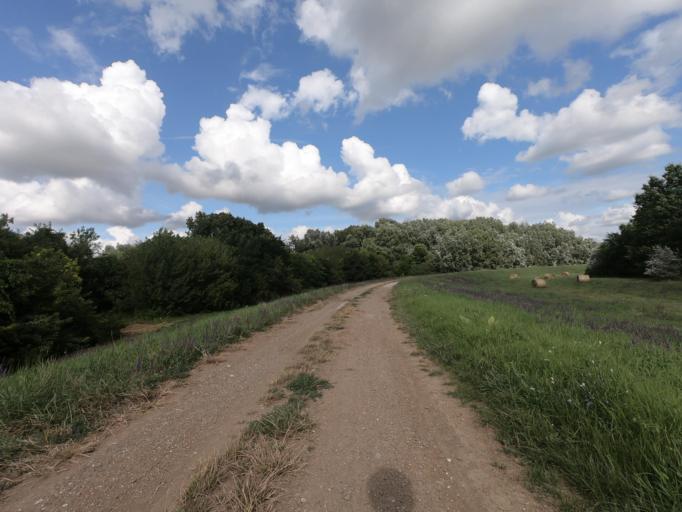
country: HU
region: Heves
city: Poroszlo
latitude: 47.6895
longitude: 20.7017
